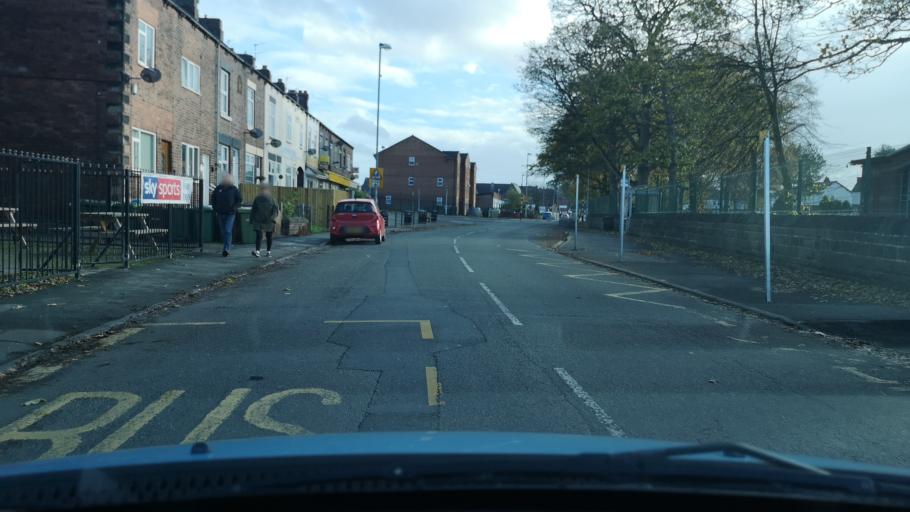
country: GB
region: England
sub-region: City and Borough of Wakefield
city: Crofton
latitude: 53.6568
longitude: -1.4289
